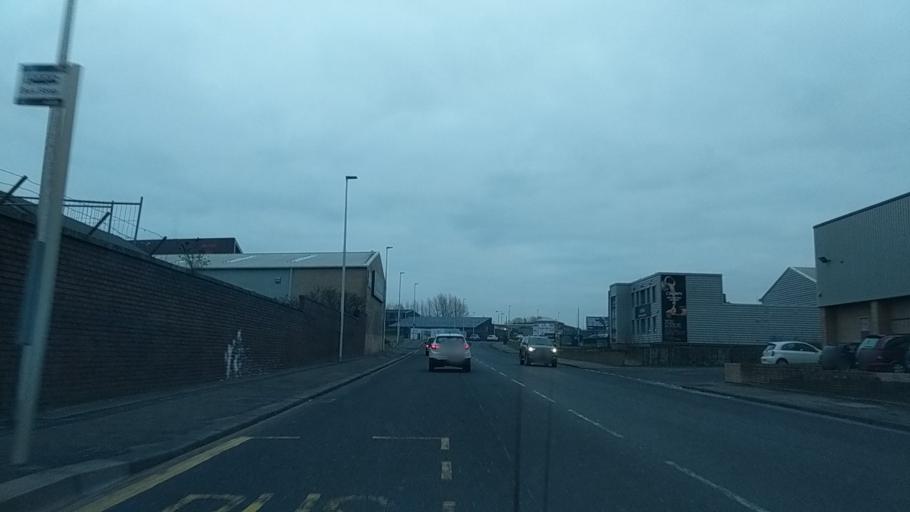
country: GB
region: Scotland
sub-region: South Lanarkshire
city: Rutherglen
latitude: 55.8372
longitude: -4.2290
